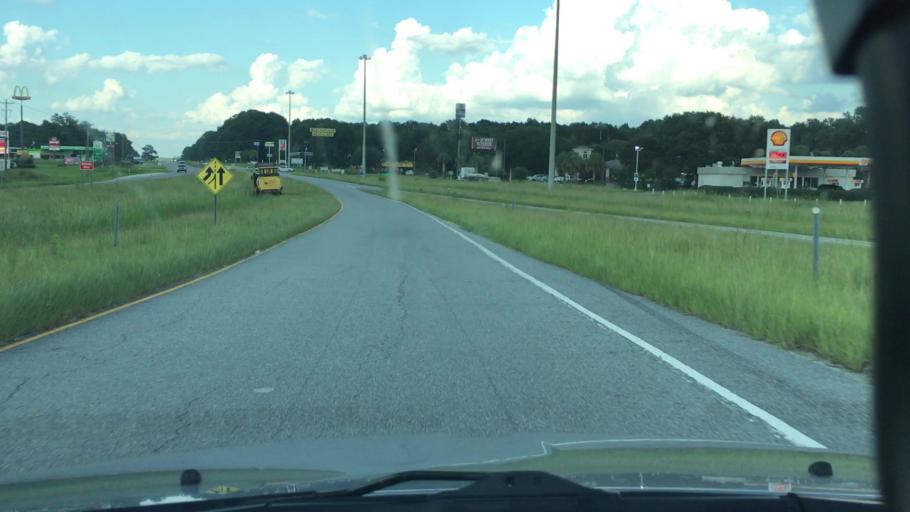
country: US
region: South Carolina
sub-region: Hampton County
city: Yemassee
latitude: 32.6317
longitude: -80.8783
